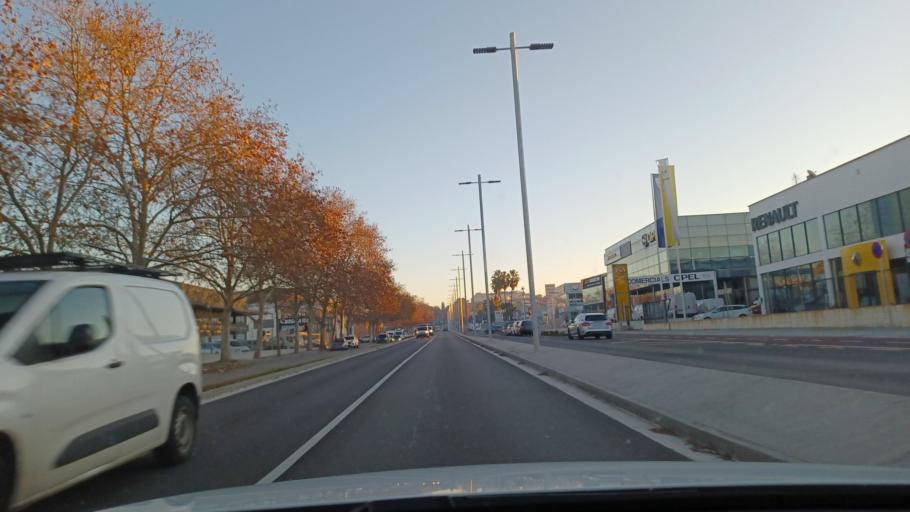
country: ES
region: Catalonia
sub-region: Provincia de Barcelona
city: Vilafranca del Penedes
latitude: 41.3356
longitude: 1.6856
